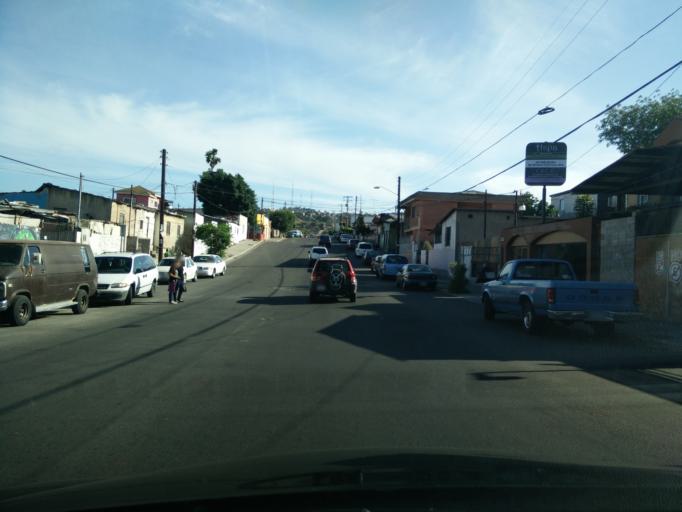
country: MX
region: Baja California
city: Tijuana
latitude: 32.5261
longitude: -117.0412
